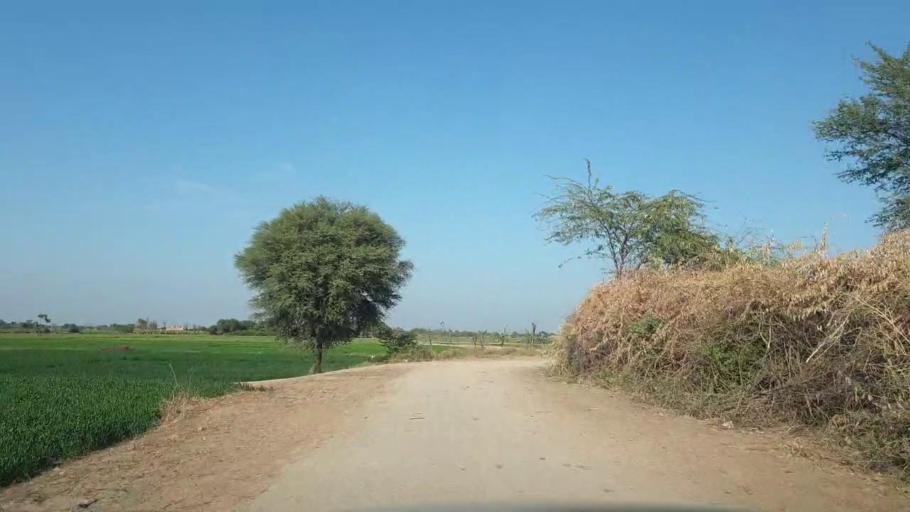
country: PK
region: Sindh
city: Tando Adam
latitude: 25.6780
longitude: 68.6872
